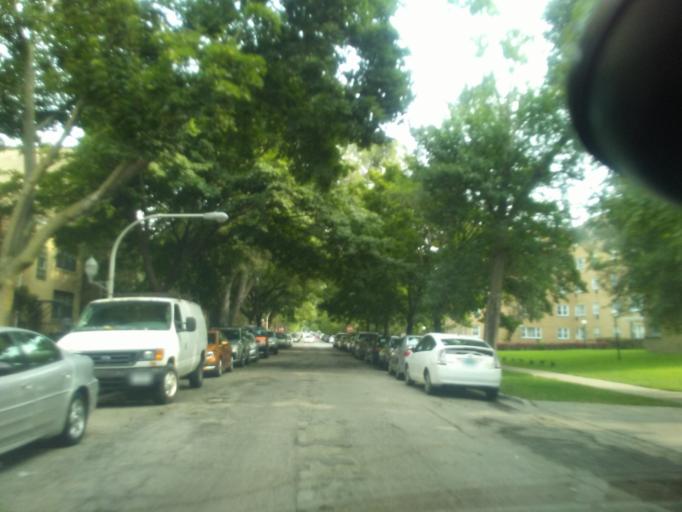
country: US
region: Illinois
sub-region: Cook County
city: Evanston
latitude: 41.9933
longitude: -87.6824
